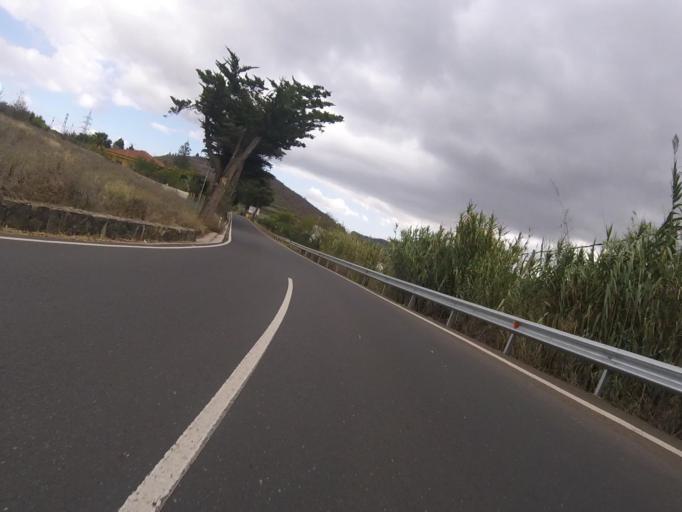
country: ES
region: Canary Islands
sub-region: Provincia de Las Palmas
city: Vega de San Mateo
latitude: 28.0083
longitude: -15.5460
